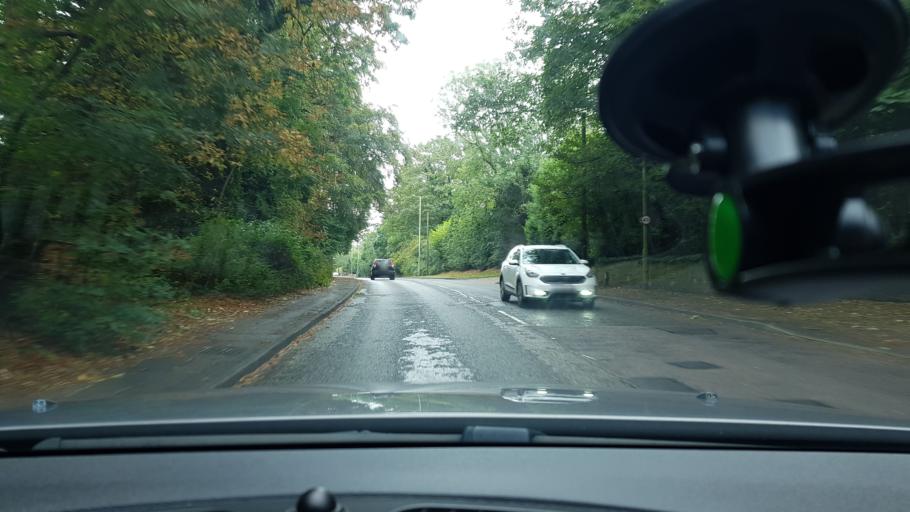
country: GB
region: England
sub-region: Hertfordshire
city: Chorleywood
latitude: 51.6524
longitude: -0.4848
